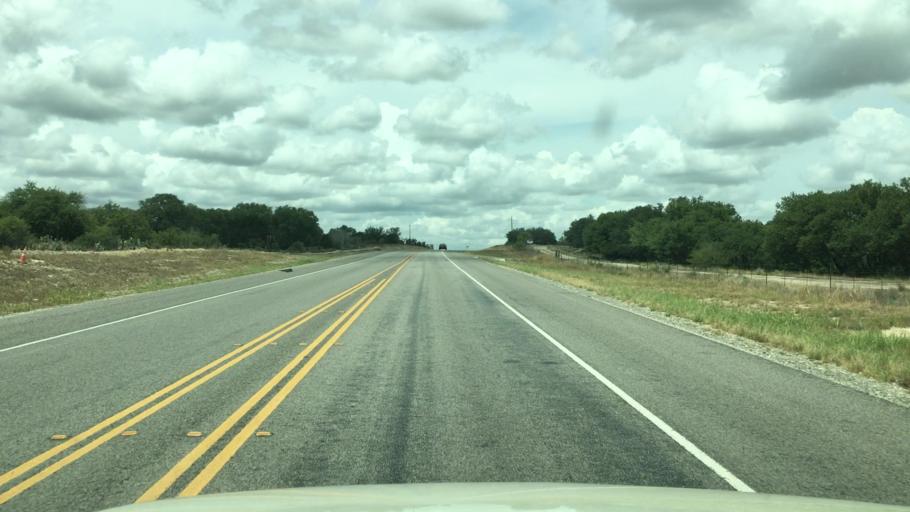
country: US
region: Texas
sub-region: McCulloch County
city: Brady
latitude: 31.0323
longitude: -99.2322
